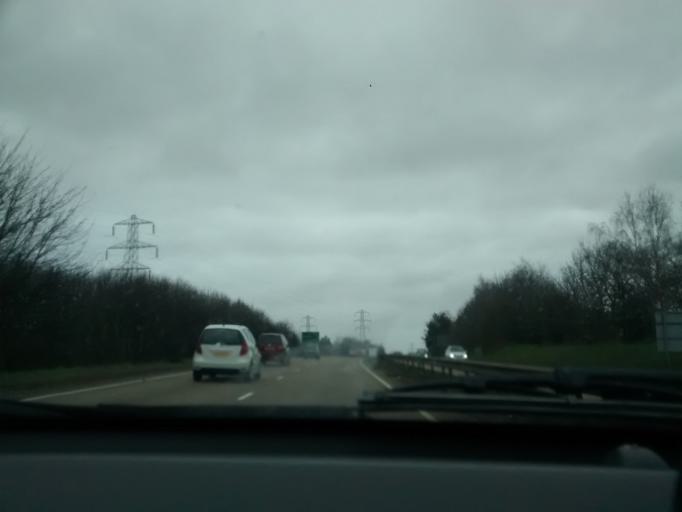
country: GB
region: England
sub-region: Suffolk
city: Bramford
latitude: 52.0326
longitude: 1.1100
